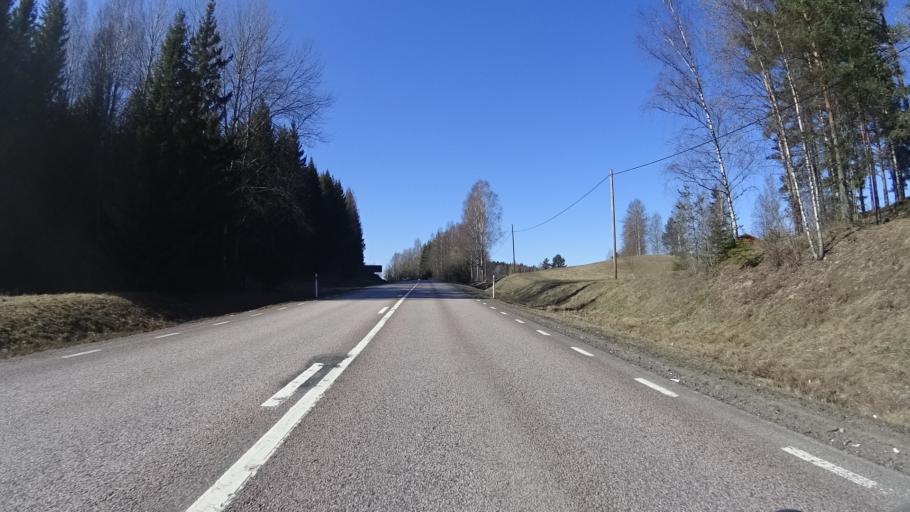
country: SE
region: Vaermland
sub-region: Karlstads Kommun
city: Edsvalla
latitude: 59.5346
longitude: 13.1095
